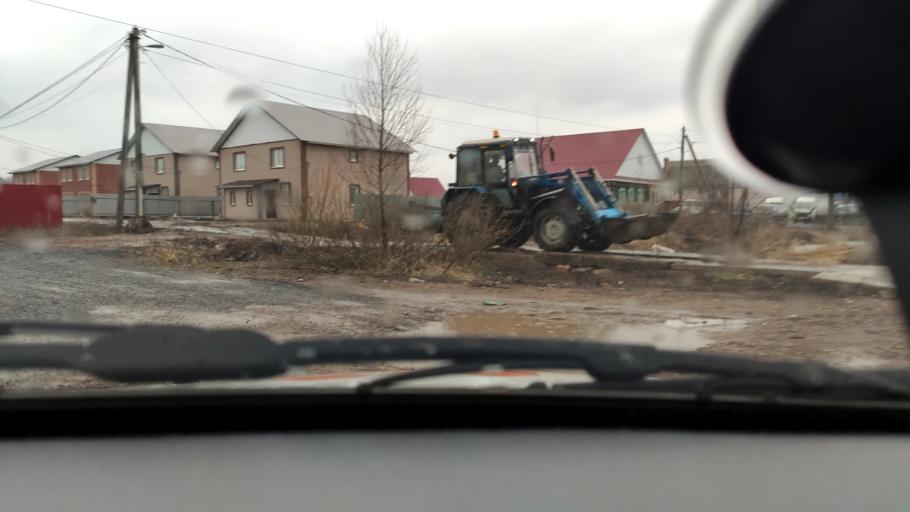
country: RU
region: Bashkortostan
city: Mikhaylovka
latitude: 54.7848
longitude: 55.8156
